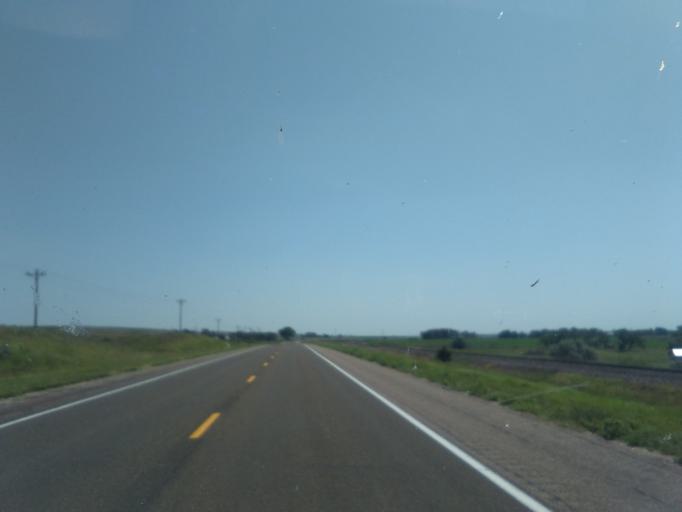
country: US
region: Nebraska
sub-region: Dundy County
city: Benkelman
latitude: 40.1239
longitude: -101.3678
